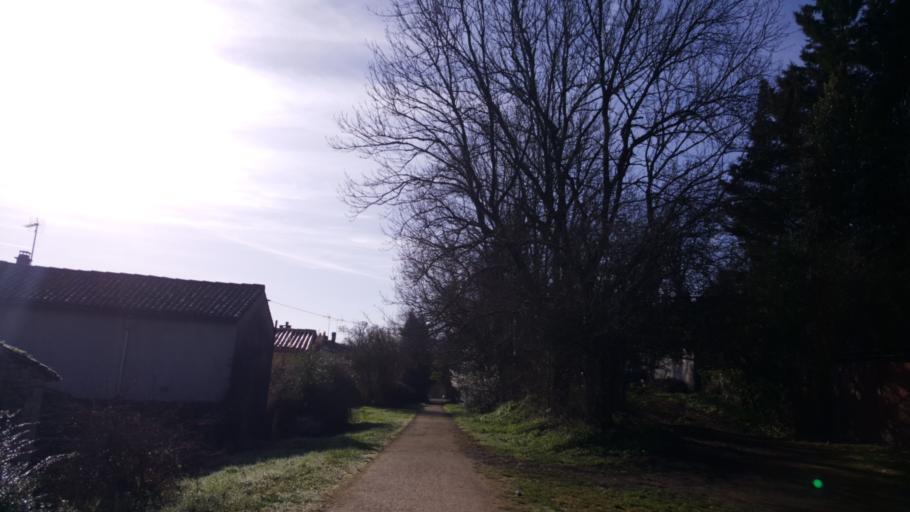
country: FR
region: Poitou-Charentes
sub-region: Departement des Deux-Sevres
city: Melle
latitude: 46.2215
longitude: -0.1514
